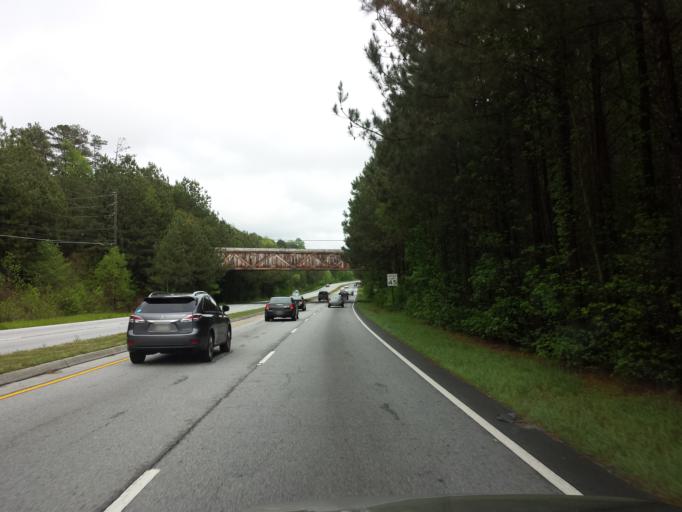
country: US
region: Georgia
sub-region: Cobb County
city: Mableton
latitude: 33.8566
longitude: -84.5684
